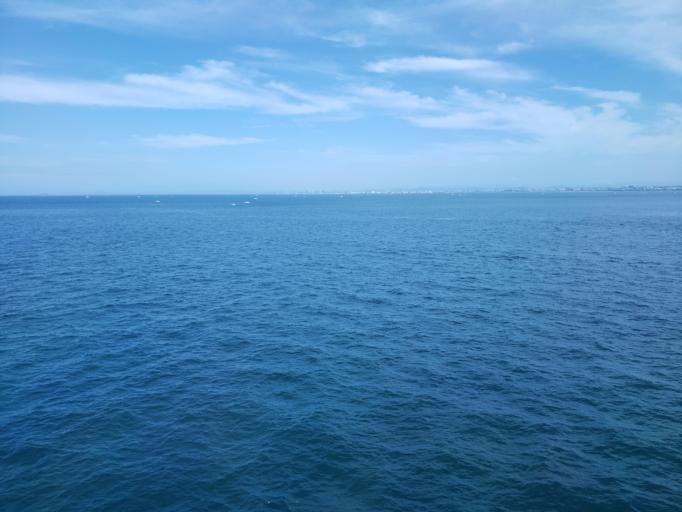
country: JP
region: Hyogo
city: Akashi
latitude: 34.6138
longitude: 134.9356
